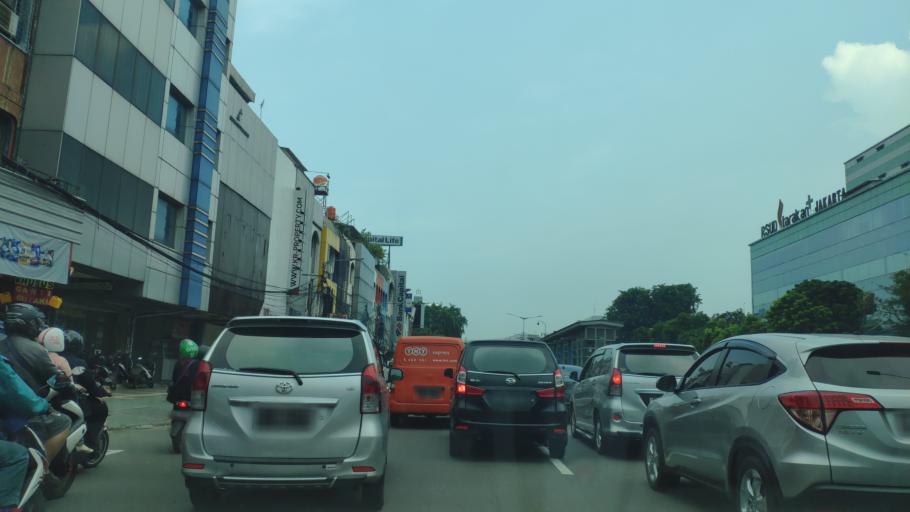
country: ID
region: Jakarta Raya
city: Jakarta
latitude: -6.1712
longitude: 106.8096
